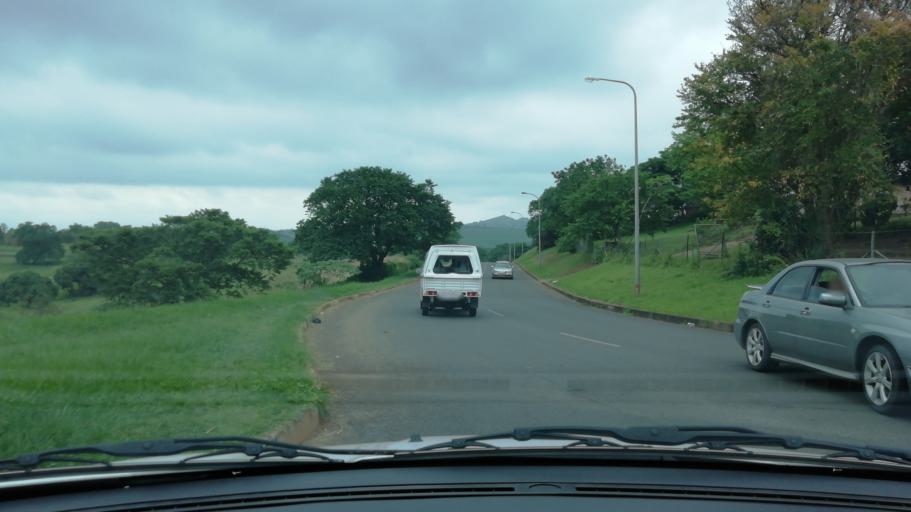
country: ZA
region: KwaZulu-Natal
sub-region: uThungulu District Municipality
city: Empangeni
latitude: -28.7472
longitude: 31.8874
